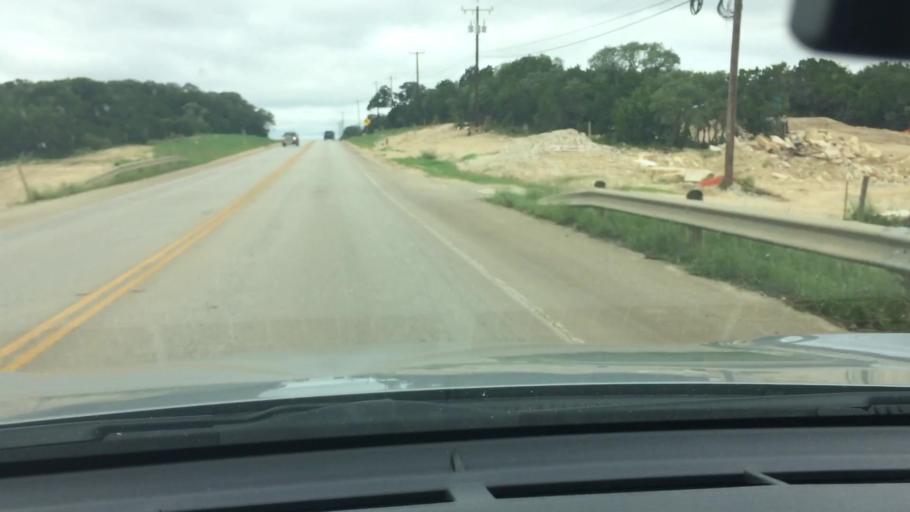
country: US
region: Texas
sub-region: Comal County
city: Garden Ridge
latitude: 29.6422
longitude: -98.3863
